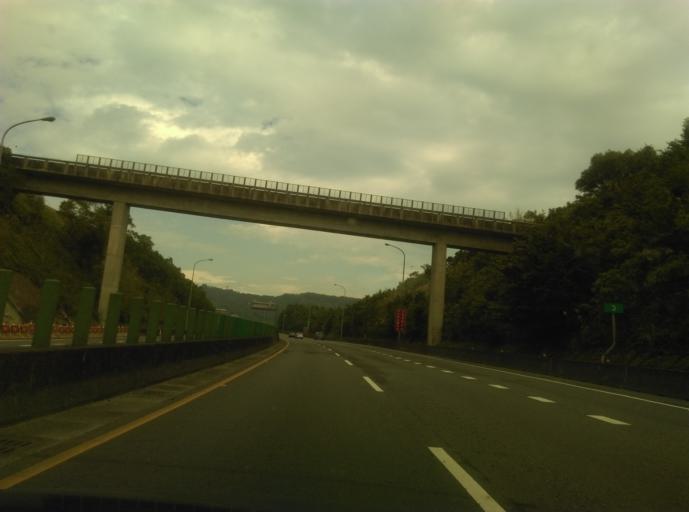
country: TW
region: Taiwan
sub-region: Keelung
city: Keelung
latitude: 25.1177
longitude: 121.6961
